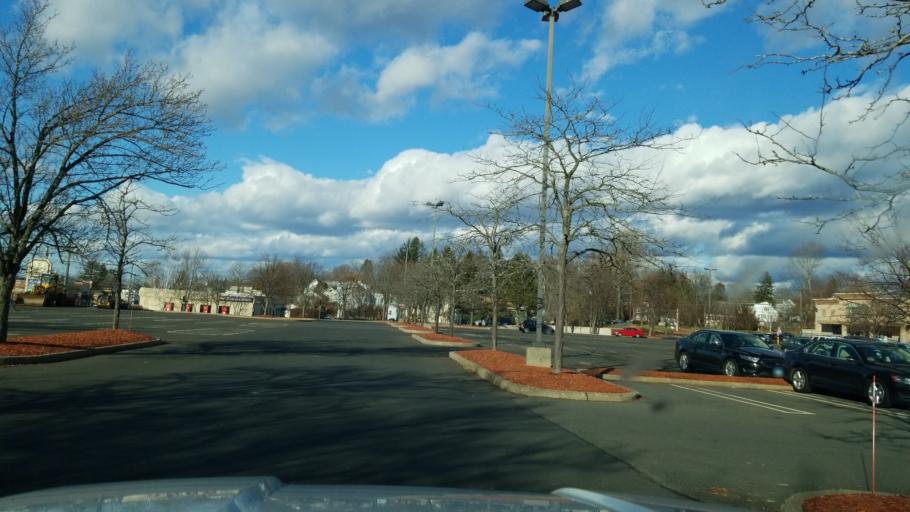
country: US
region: Connecticut
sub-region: Middlesex County
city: Middletown
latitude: 41.5461
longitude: -72.6387
